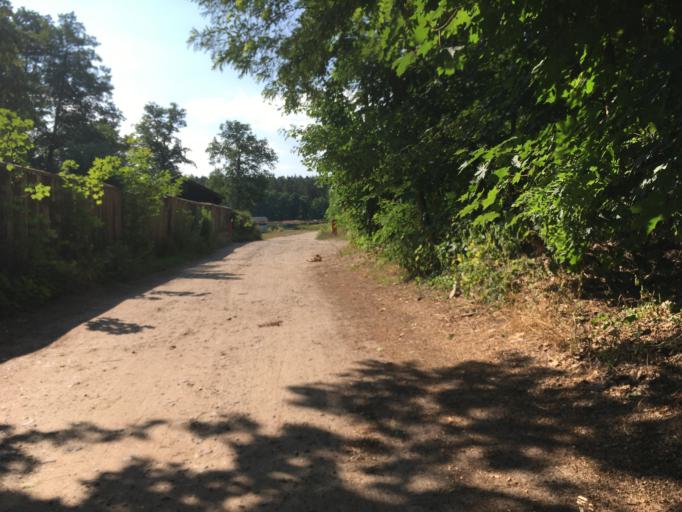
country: DE
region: Brandenburg
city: Templin
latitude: 53.1299
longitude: 13.5500
